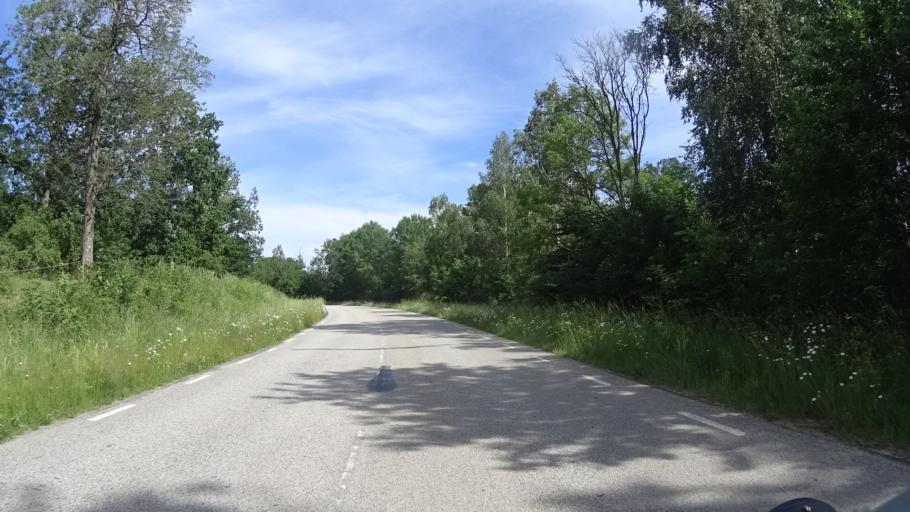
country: SE
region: Kalmar
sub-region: Vasterviks Kommun
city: Overum
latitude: 57.9063
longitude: 16.1759
